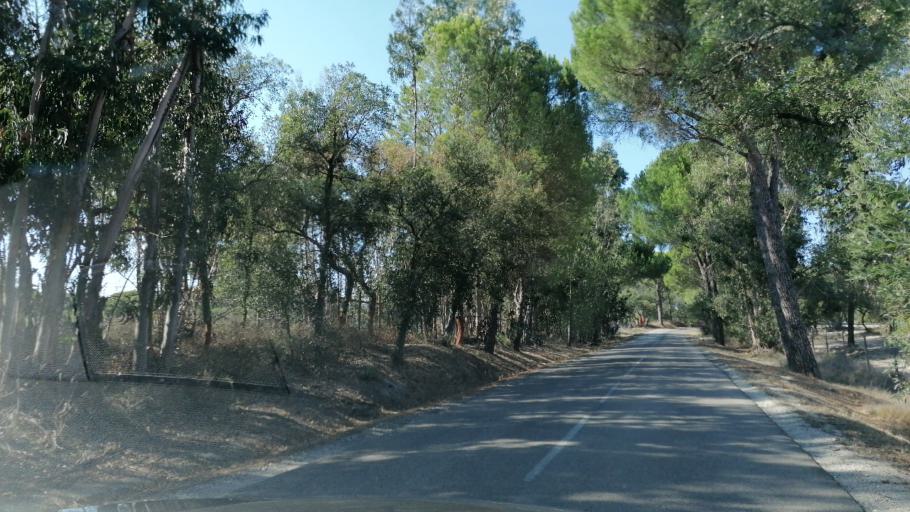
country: PT
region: Santarem
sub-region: Coruche
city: Coruche
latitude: 38.8050
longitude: -8.5790
